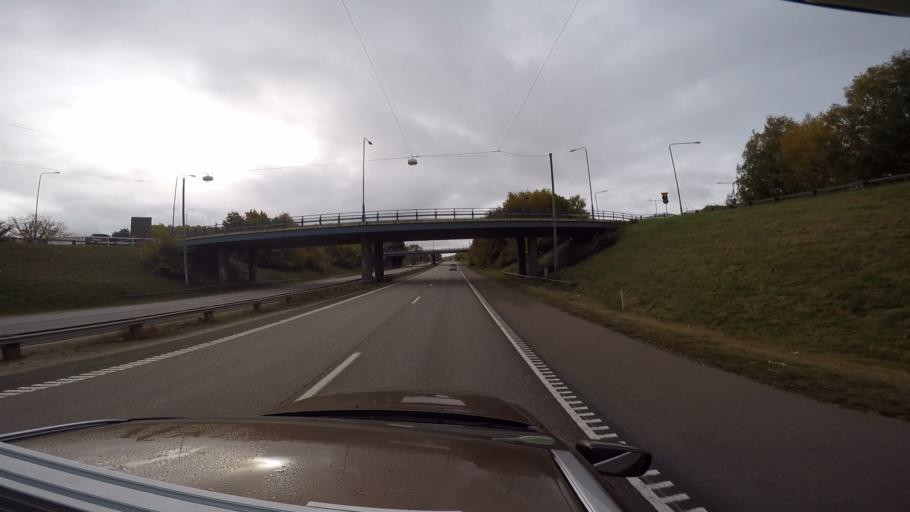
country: SE
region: Vaestra Goetaland
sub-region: Goteborg
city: Majorna
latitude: 57.6603
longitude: 11.9355
